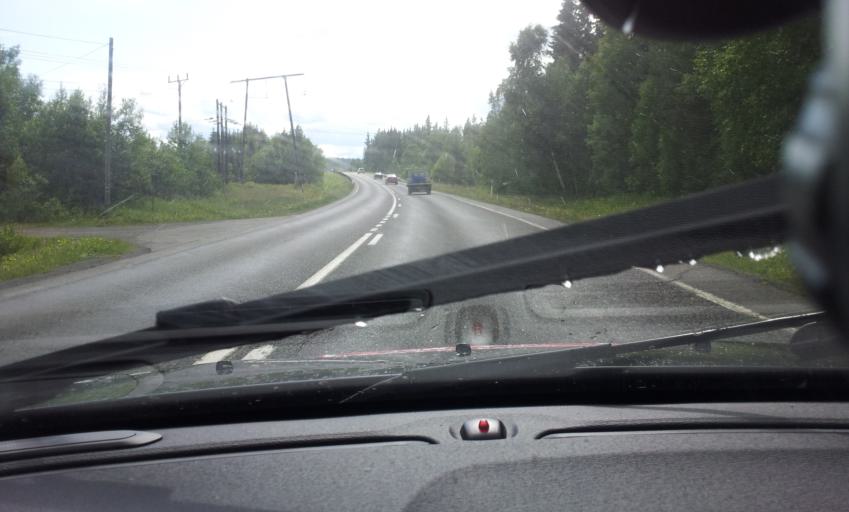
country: SE
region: Jaemtland
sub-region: Krokoms Kommun
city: Valla
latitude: 63.3361
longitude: 13.9807
